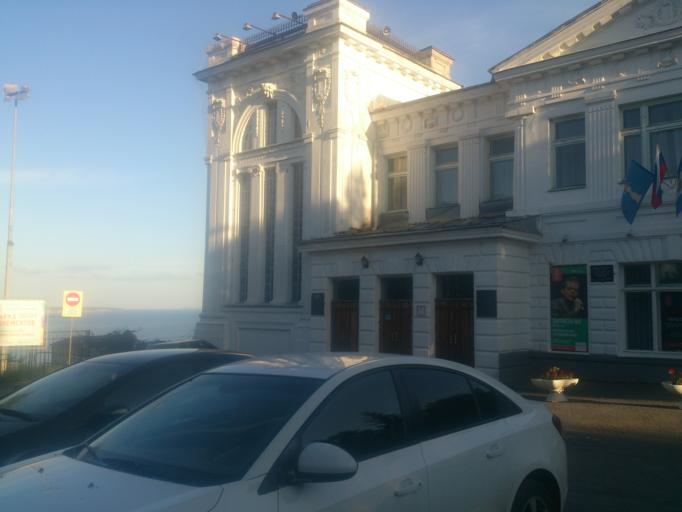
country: RU
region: Ulyanovsk
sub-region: Ulyanovskiy Rayon
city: Ulyanovsk
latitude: 54.3133
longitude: 48.4047
